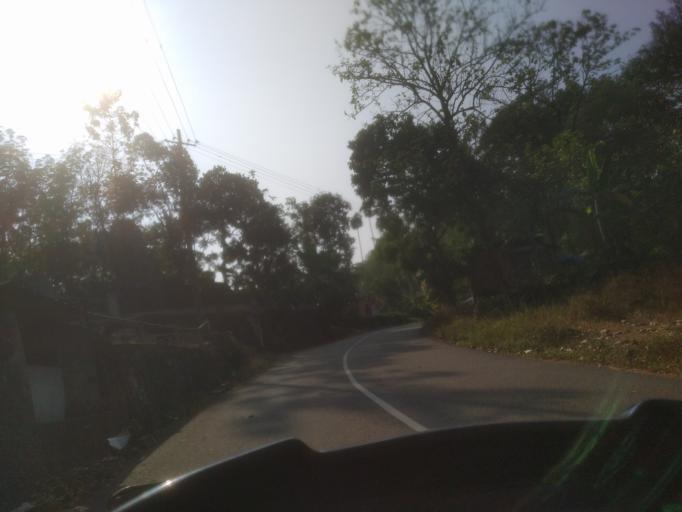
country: IN
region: Kerala
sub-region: Ernakulam
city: Piravam
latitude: 9.8692
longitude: 76.5414
